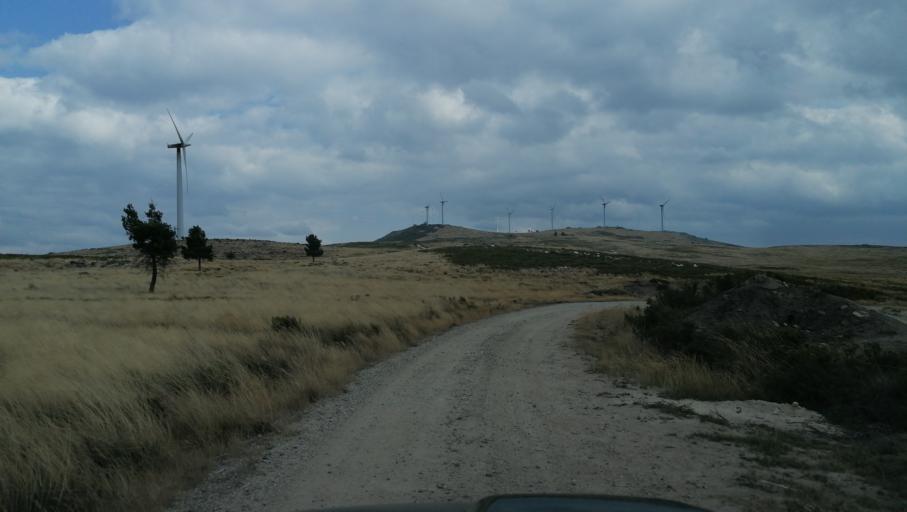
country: PT
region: Vila Real
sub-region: Vila Pouca de Aguiar
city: Vila Pouca de Aguiar
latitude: 41.5373
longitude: -7.7075
